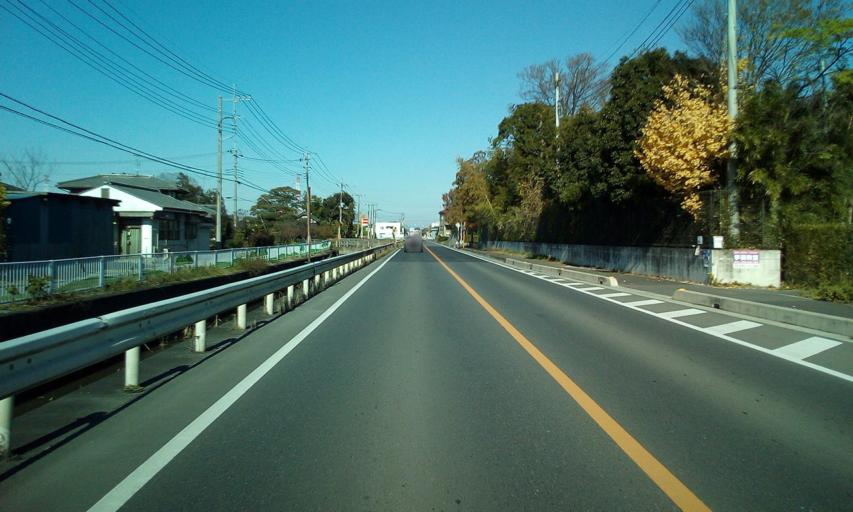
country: JP
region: Saitama
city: Kasukabe
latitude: 35.9937
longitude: 139.7962
